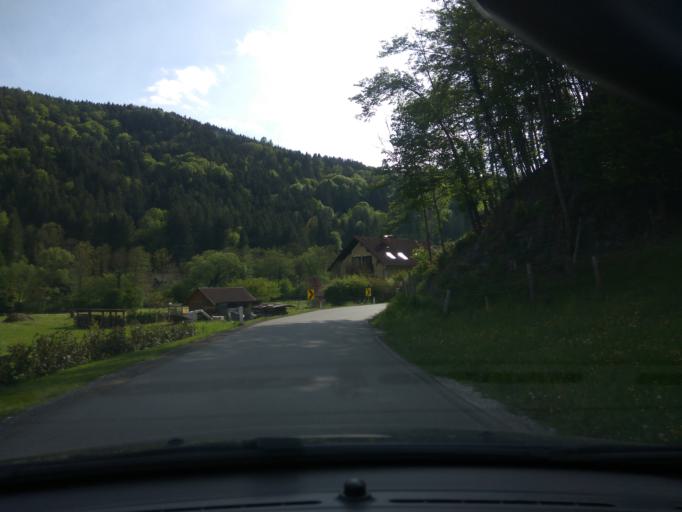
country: AT
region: Styria
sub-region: Politischer Bezirk Voitsberg
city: Voitsberg
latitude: 47.0210
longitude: 15.1756
